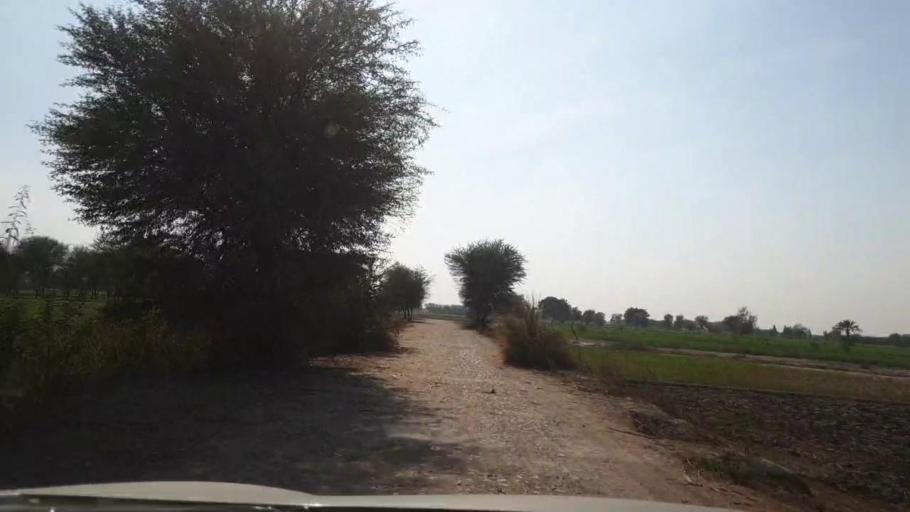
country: PK
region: Sindh
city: Berani
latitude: 25.7152
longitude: 68.7511
